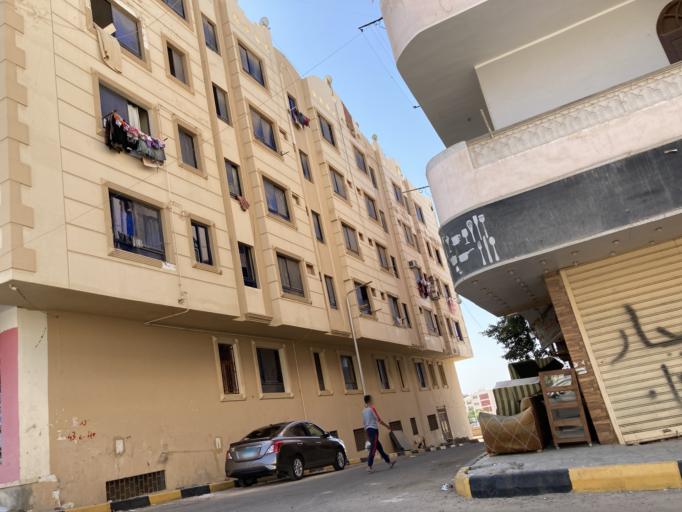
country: EG
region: Red Sea
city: Hurghada
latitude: 27.2504
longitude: 33.8322
